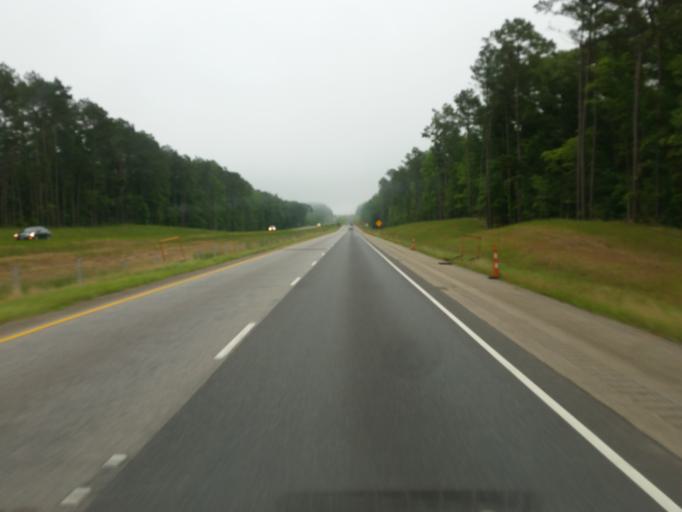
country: US
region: Louisiana
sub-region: Webster Parish
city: Minden
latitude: 32.5664
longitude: -93.1811
